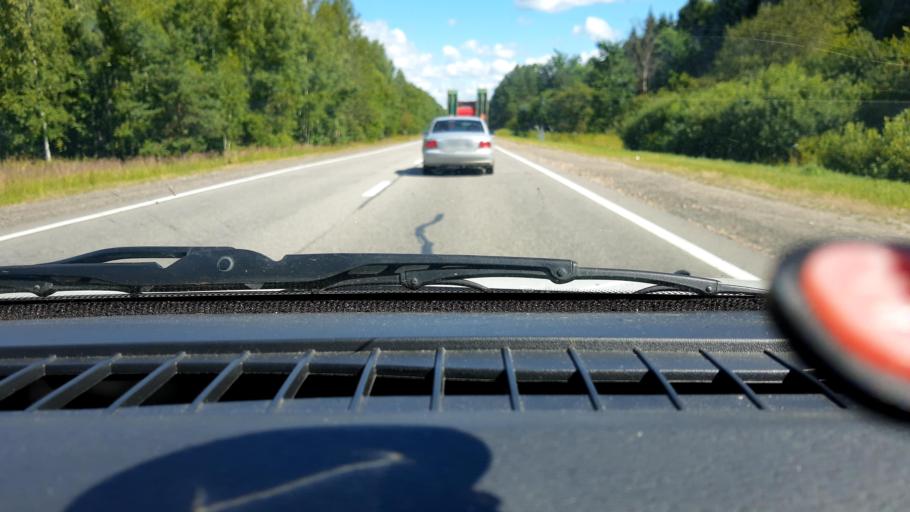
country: RU
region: Nizjnij Novgorod
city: Surovatikha
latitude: 55.5829
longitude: 43.9747
